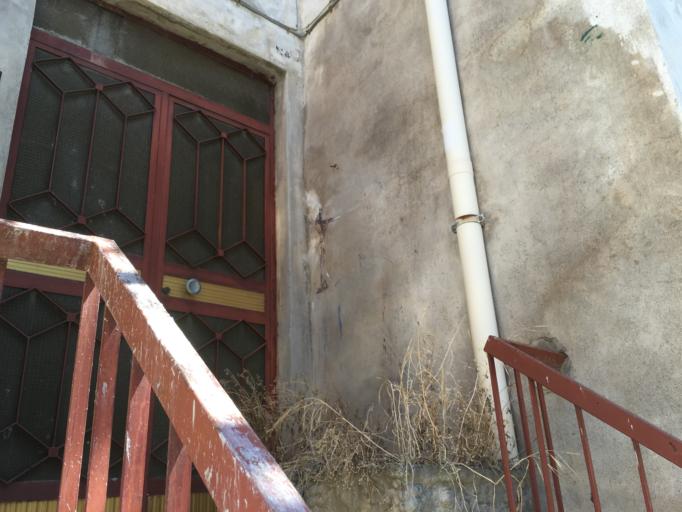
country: IT
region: Calabria
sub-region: Provincia di Cosenza
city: Castrovillari
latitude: 39.8092
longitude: 16.2038
